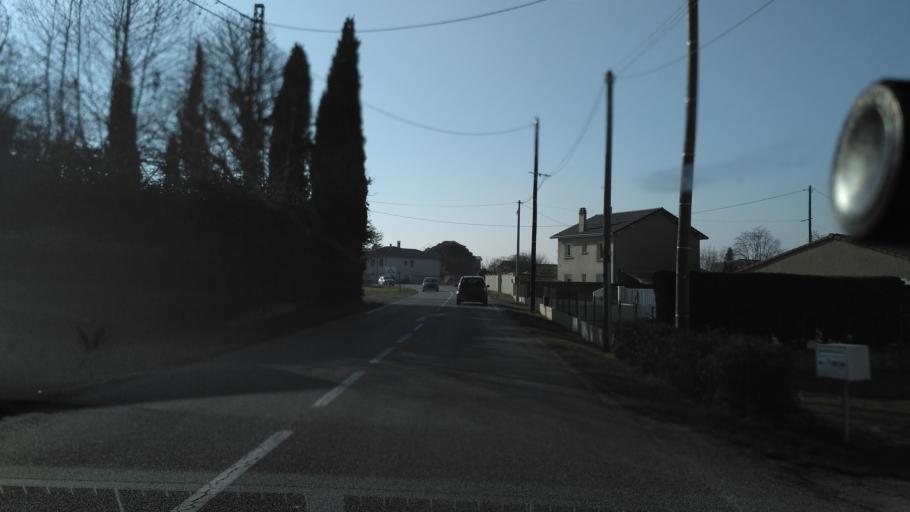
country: FR
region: Rhone-Alpes
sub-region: Departement de la Drome
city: Mours-Saint-Eusebe
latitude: 45.0598
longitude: 5.0653
